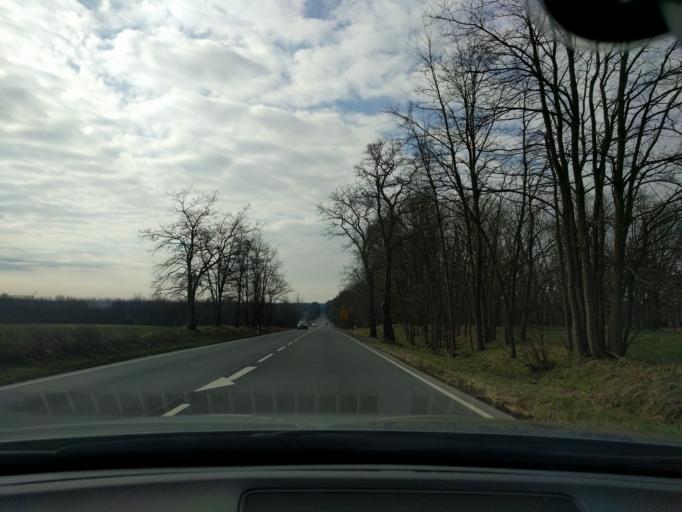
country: DE
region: Saxony-Anhalt
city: Colbitz
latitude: 52.3876
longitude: 11.6194
